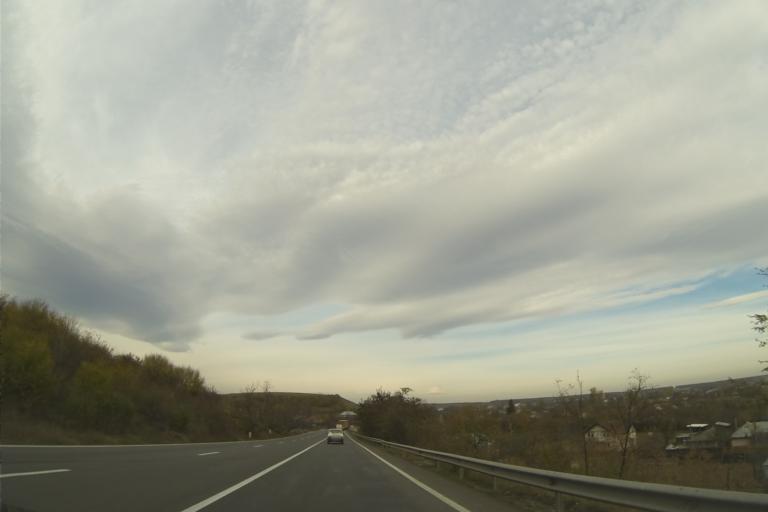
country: RO
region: Olt
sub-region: Comuna Scornicesti
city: Margineni Slobozia
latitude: 44.5390
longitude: 24.5381
